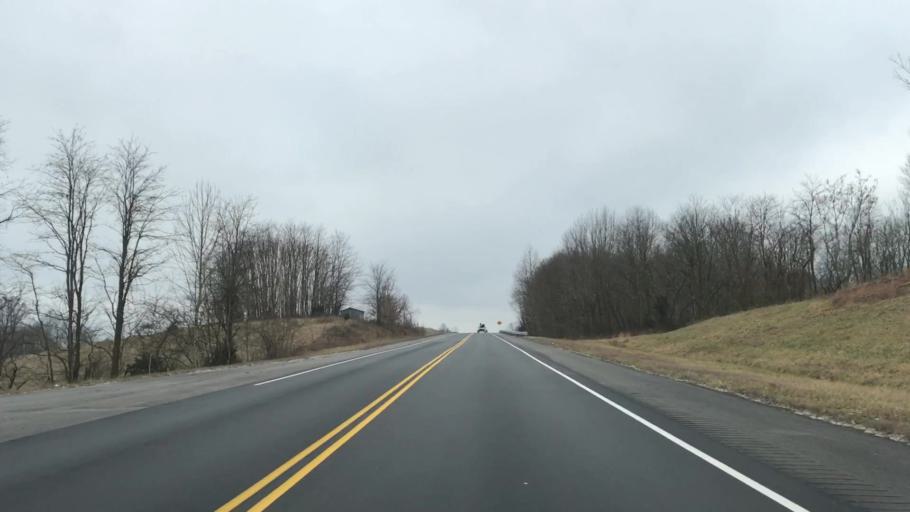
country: US
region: Kentucky
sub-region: Adair County
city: Columbia
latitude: 36.9712
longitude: -85.4252
